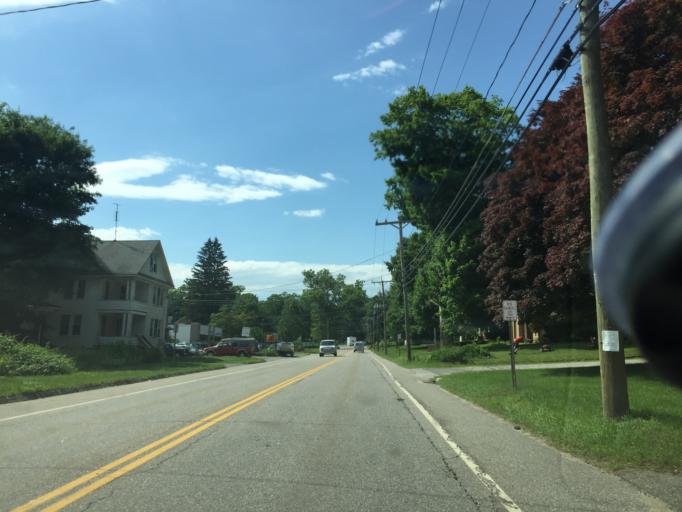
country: US
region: Connecticut
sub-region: Litchfield County
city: West Torrington
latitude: 41.8165
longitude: -73.1414
